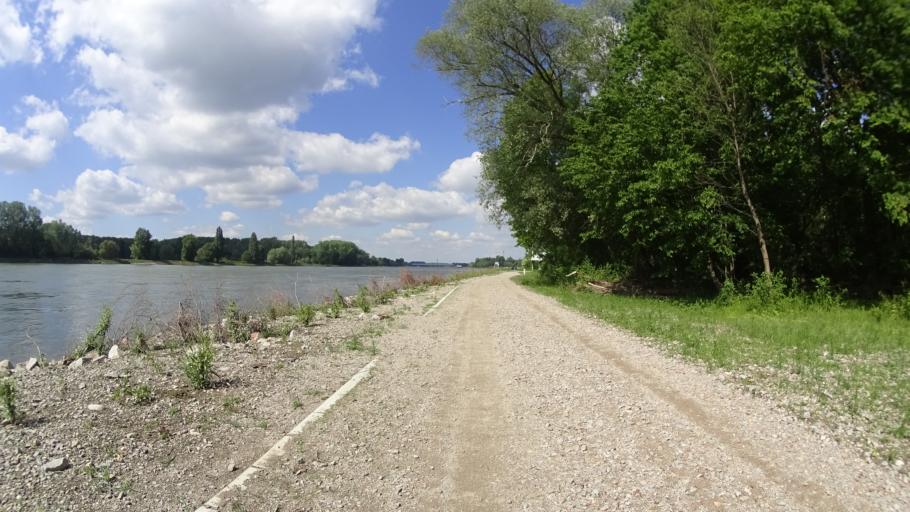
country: DE
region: Baden-Wuerttemberg
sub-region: Karlsruhe Region
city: Rheinstetten
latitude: 49.0100
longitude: 8.2977
